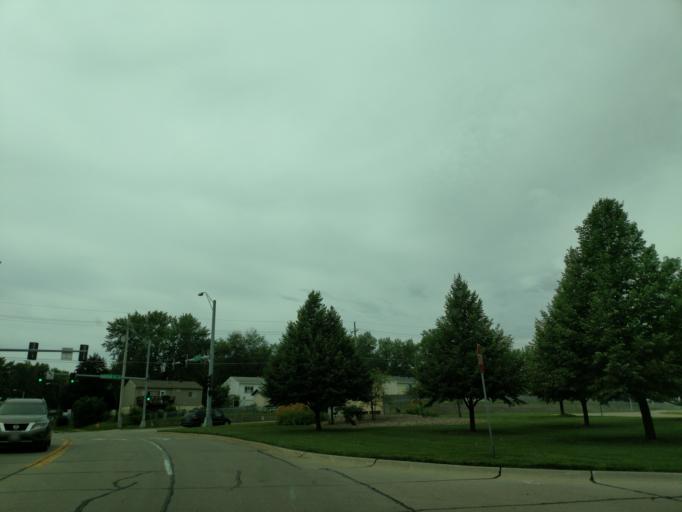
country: US
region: Nebraska
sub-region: Sarpy County
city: La Vista
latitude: 41.1913
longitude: -96.0338
